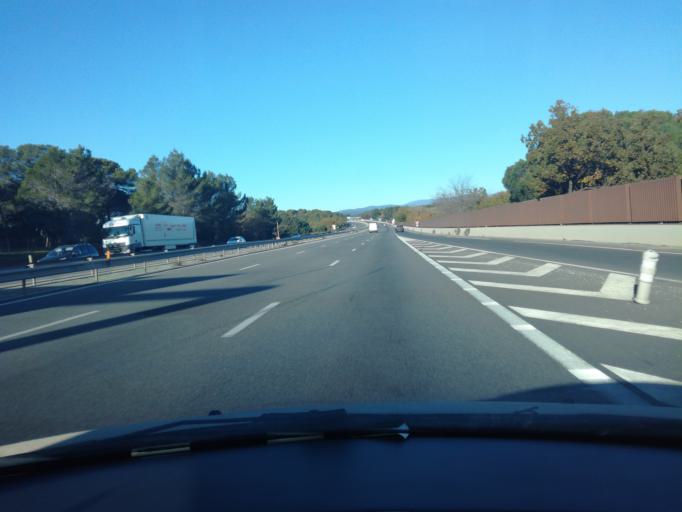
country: FR
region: Provence-Alpes-Cote d'Azur
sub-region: Departement du Var
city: Puget-sur-Argens
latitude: 43.4611
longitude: 6.6843
